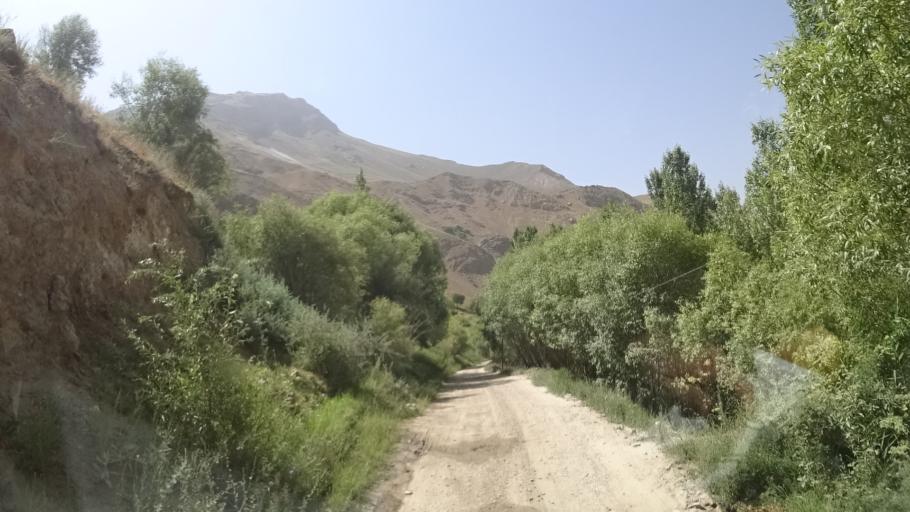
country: TJ
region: Gorno-Badakhshan
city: Khorugh
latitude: 37.1876
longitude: 71.4631
